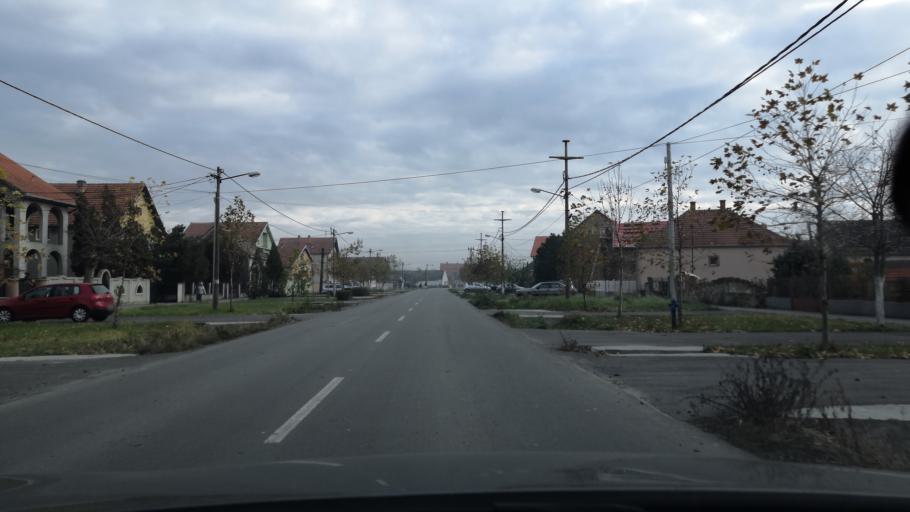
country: RS
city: Ugrinovci
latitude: 44.8787
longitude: 20.1771
